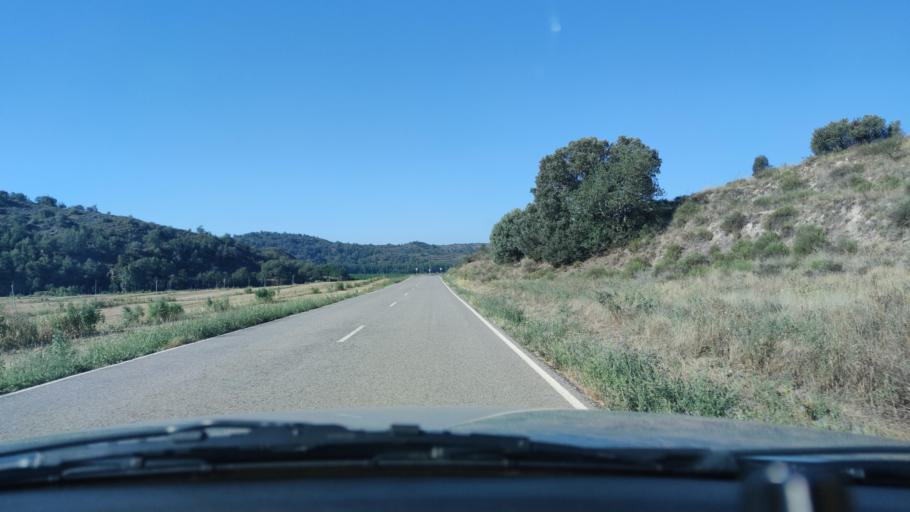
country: ES
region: Catalonia
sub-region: Provincia de Lleida
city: Ponts
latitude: 41.8962
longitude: 1.2368
